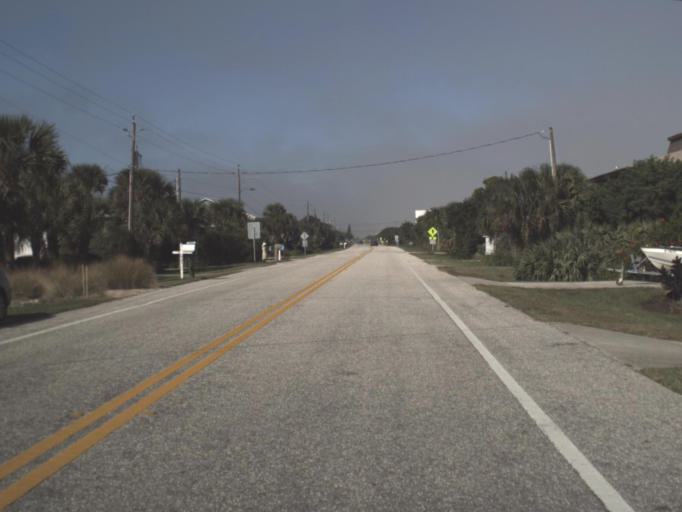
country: US
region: Florida
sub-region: Volusia County
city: Edgewater
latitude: 28.9438
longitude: -80.8351
